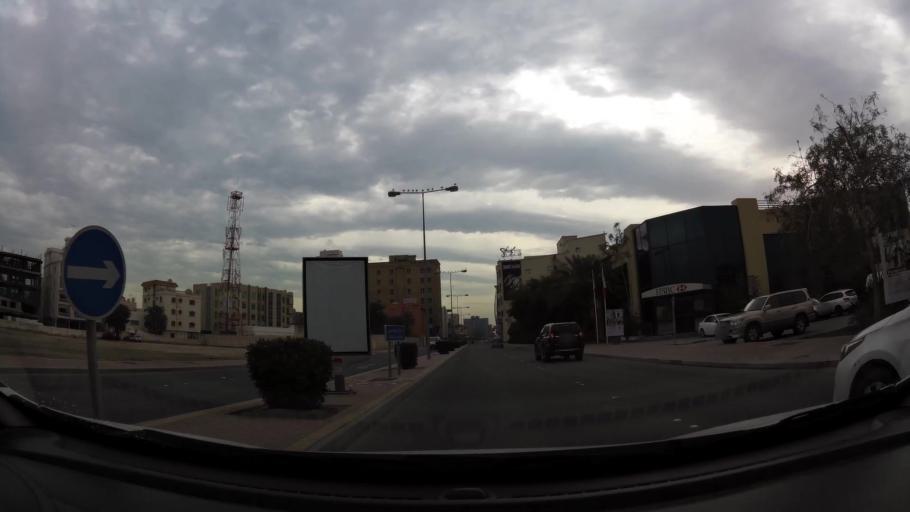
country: BH
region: Manama
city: Manama
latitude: 26.2200
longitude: 50.5854
